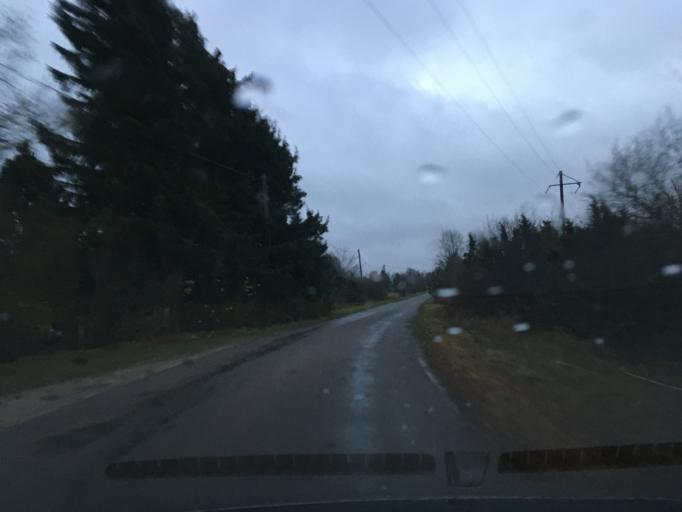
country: EE
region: Laeaene
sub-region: Lihula vald
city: Lihula
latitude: 58.5773
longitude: 23.7388
